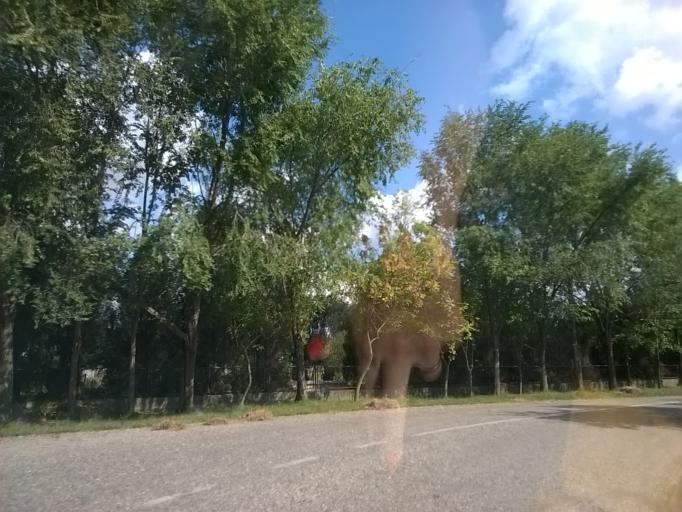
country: RS
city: Janosik
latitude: 45.1735
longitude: 21.0144
